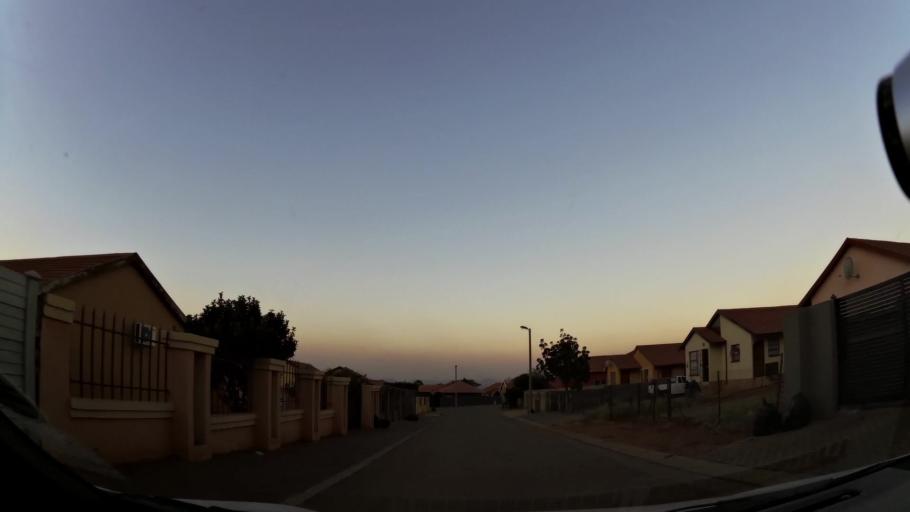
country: ZA
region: North-West
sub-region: Bojanala Platinum District Municipality
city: Rustenburg
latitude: -25.6457
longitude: 27.1991
